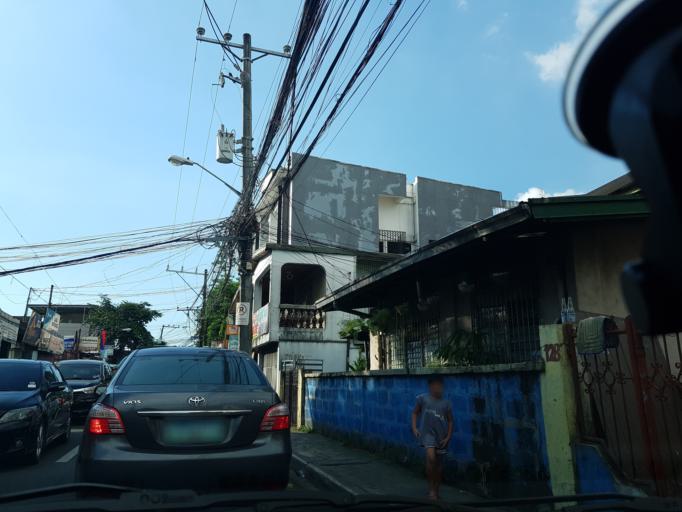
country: PH
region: Metro Manila
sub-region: Marikina
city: Calumpang
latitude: 14.6143
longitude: 121.0825
